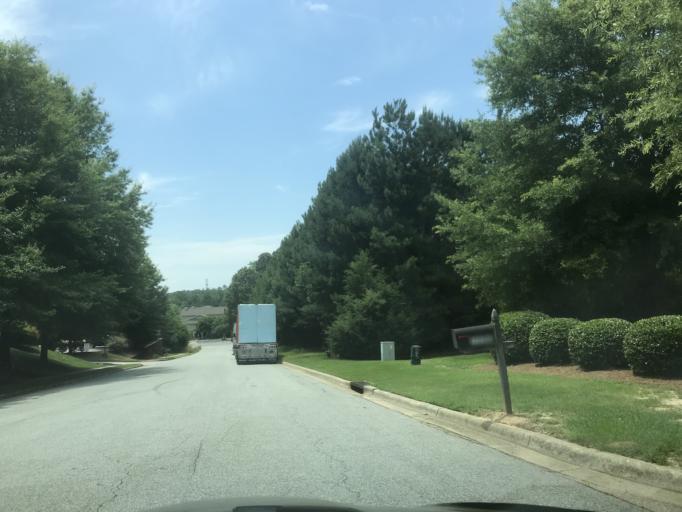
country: US
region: North Carolina
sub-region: Wake County
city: Wake Forest
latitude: 35.9447
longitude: -78.5462
